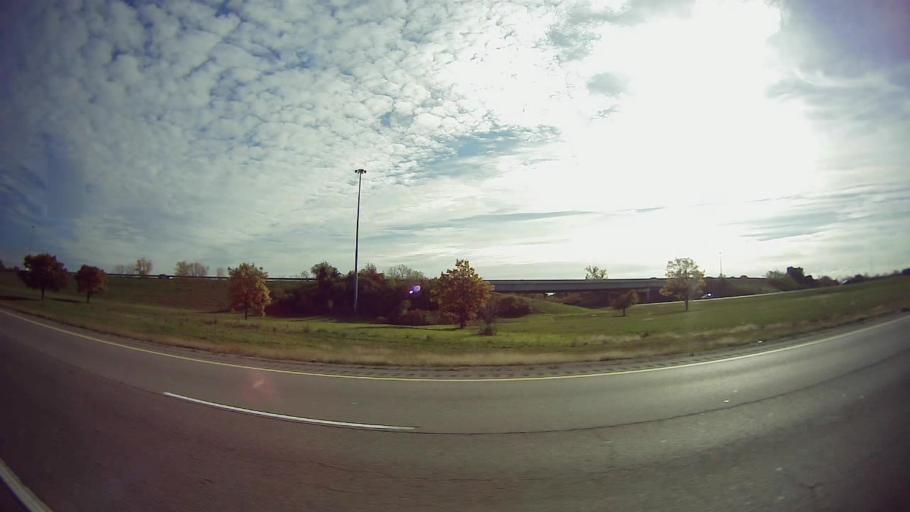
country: US
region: Michigan
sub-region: Wayne County
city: Plymouth
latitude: 42.3954
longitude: -83.4328
